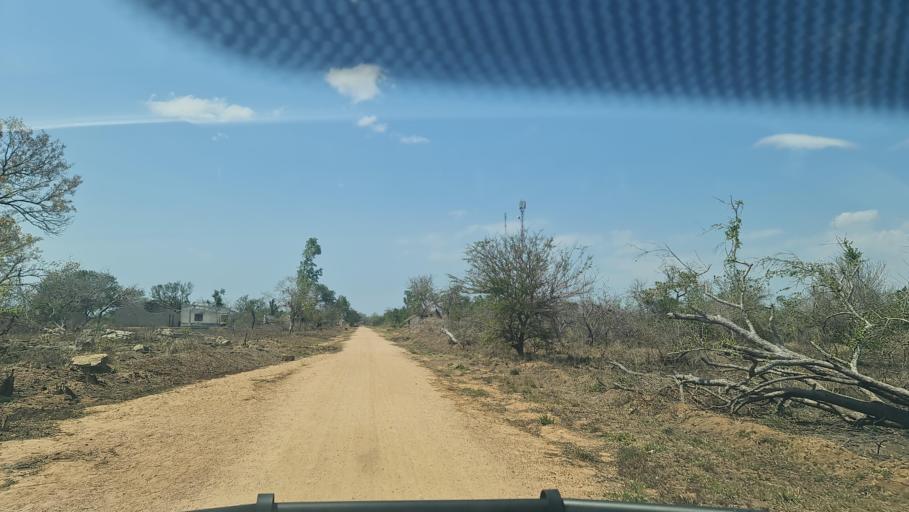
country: MZ
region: Nampula
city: Ilha de Mocambique
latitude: -15.1935
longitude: 40.5234
